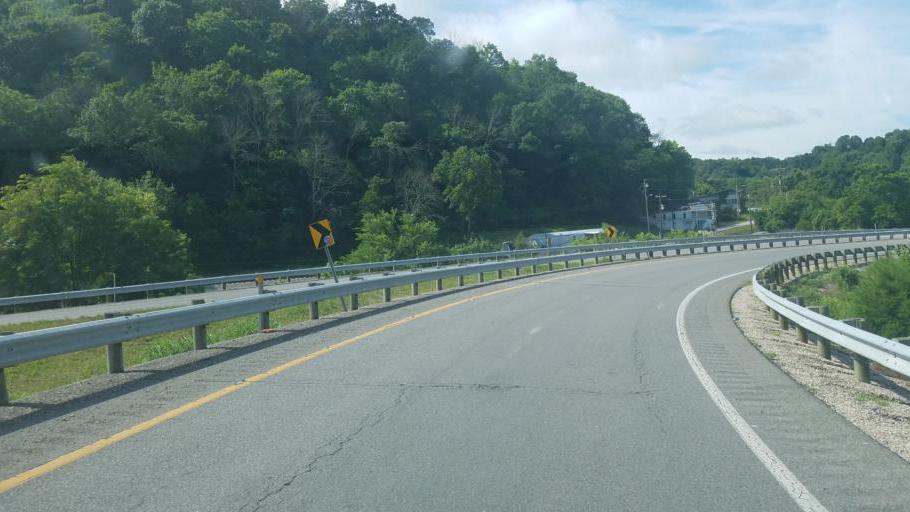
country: US
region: West Virginia
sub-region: Mason County
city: Point Pleasant
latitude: 38.8301
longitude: -82.1413
